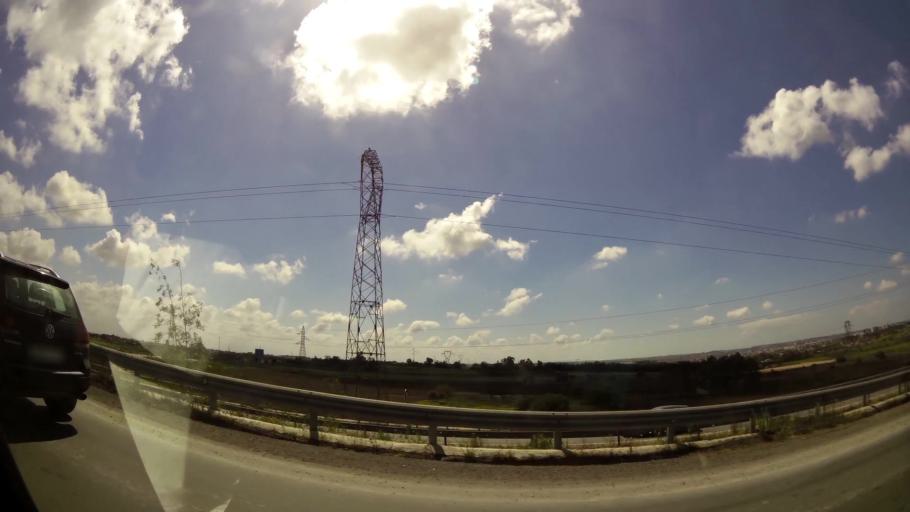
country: MA
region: Grand Casablanca
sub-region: Nouaceur
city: Bouskoura
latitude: 33.5102
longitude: -7.6123
